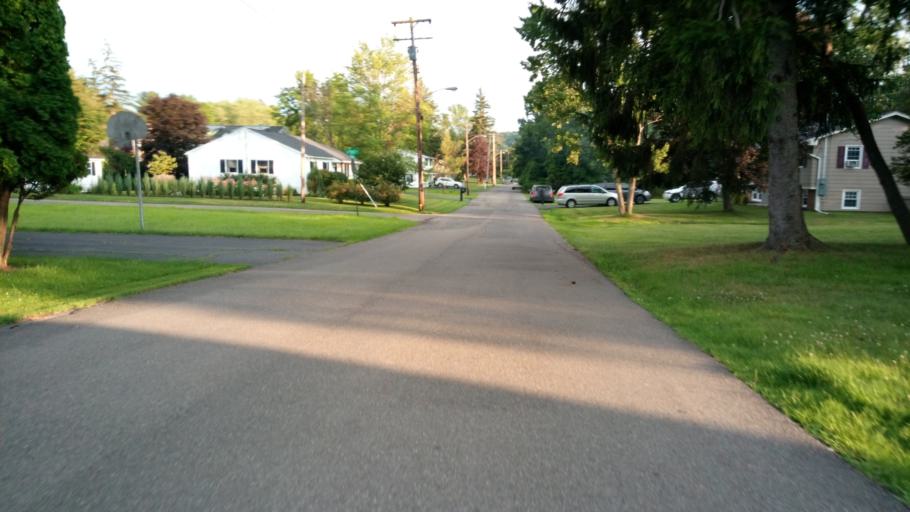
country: US
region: New York
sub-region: Chemung County
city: West Elmira
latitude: 42.0837
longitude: -76.8447
